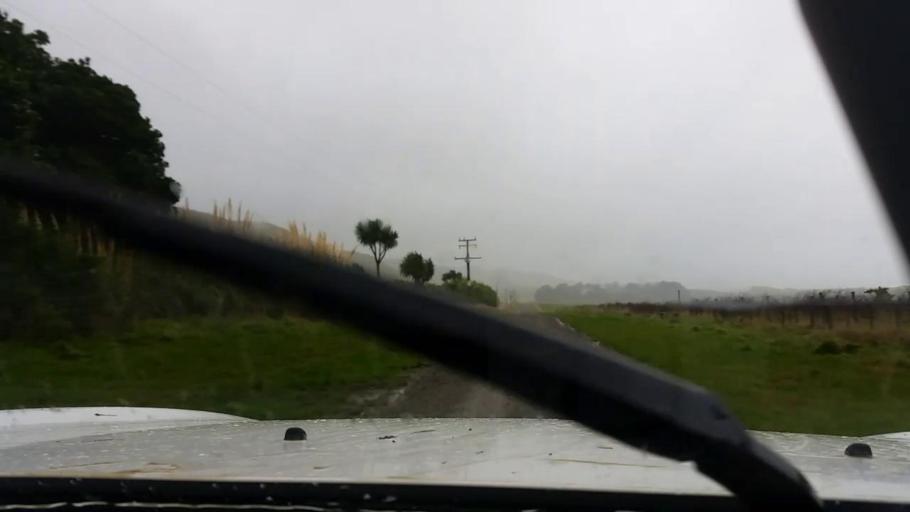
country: NZ
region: Wellington
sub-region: Masterton District
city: Masterton
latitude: -41.2577
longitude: 175.9030
